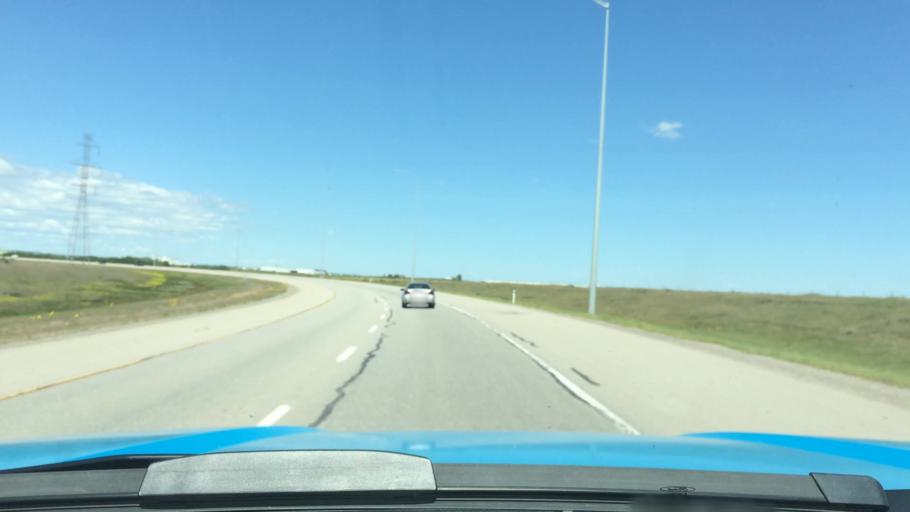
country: CA
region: Alberta
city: Chestermere
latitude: 51.1750
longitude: -113.9141
